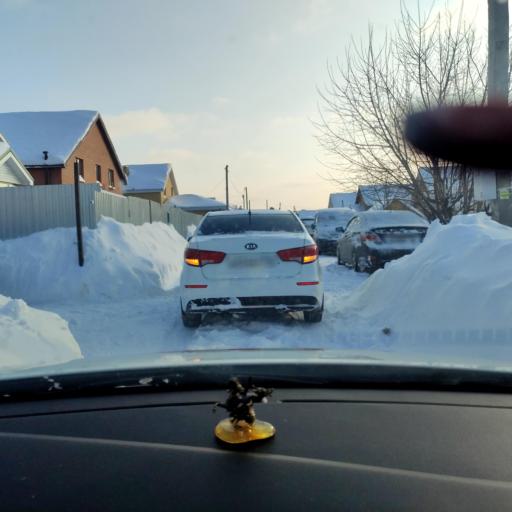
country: RU
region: Tatarstan
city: Stolbishchi
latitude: 55.7498
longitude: 49.3031
